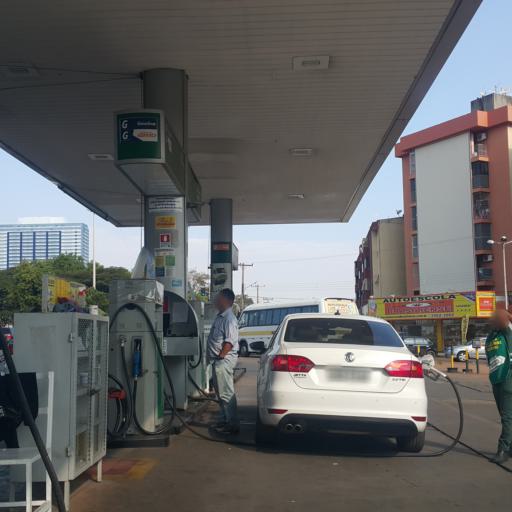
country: BR
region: Federal District
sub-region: Brasilia
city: Brasilia
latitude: -15.8366
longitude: -48.0493
